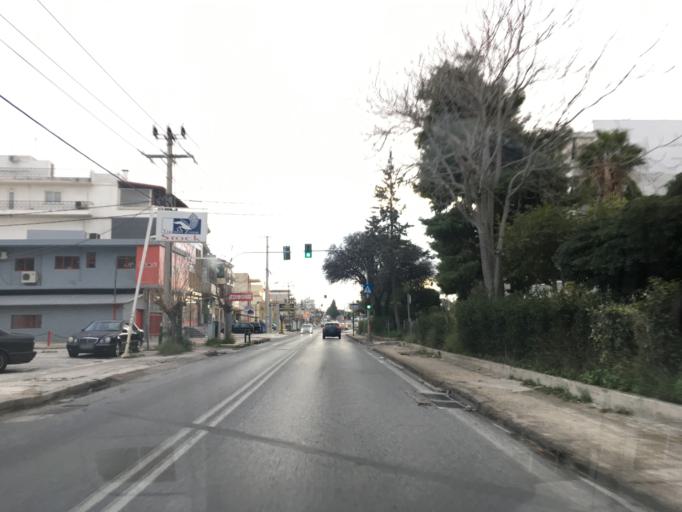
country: GR
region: Attica
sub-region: Nomarchia Athinas
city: Nea Filadelfeia
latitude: 38.0446
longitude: 23.7280
